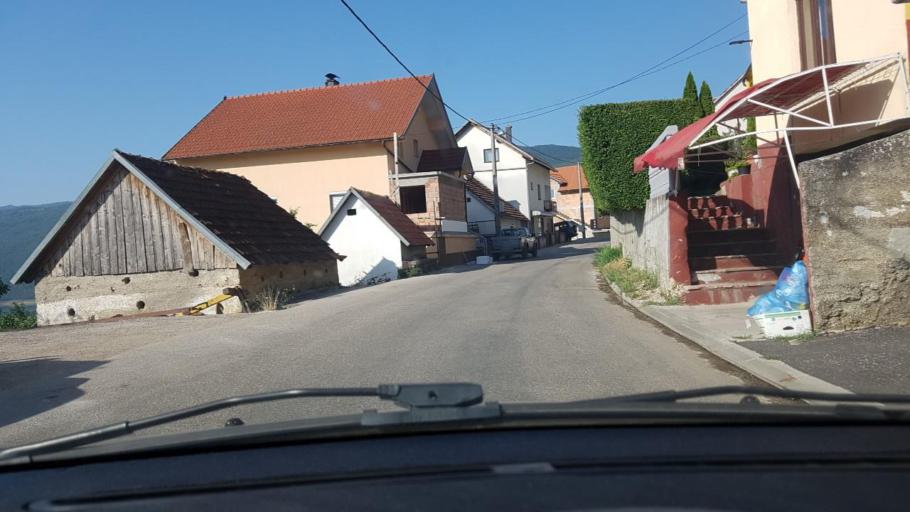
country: BA
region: Federation of Bosnia and Herzegovina
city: Rumboci
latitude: 43.8296
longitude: 17.5009
